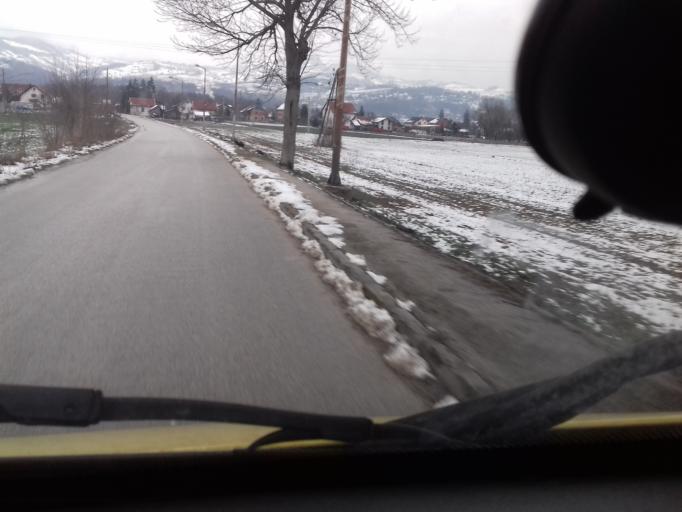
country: BA
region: Federation of Bosnia and Herzegovina
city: Vitez
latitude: 44.1604
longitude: 17.7762
